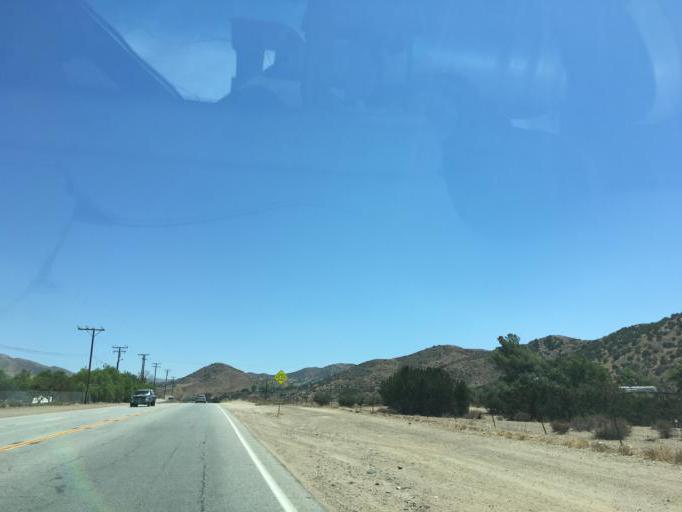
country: US
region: California
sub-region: Los Angeles County
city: Agua Dulce
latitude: 34.5199
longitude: -118.2945
